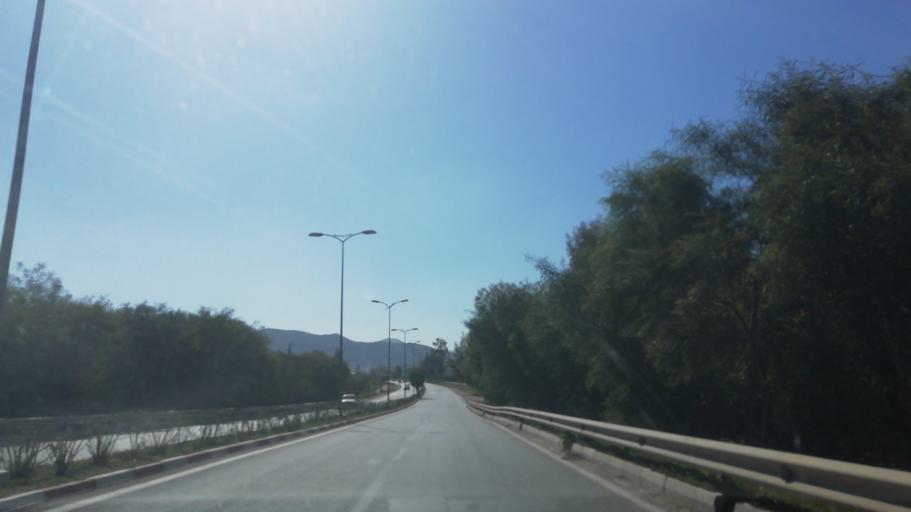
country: DZ
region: Mascara
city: Sig
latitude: 35.5381
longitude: -0.2038
